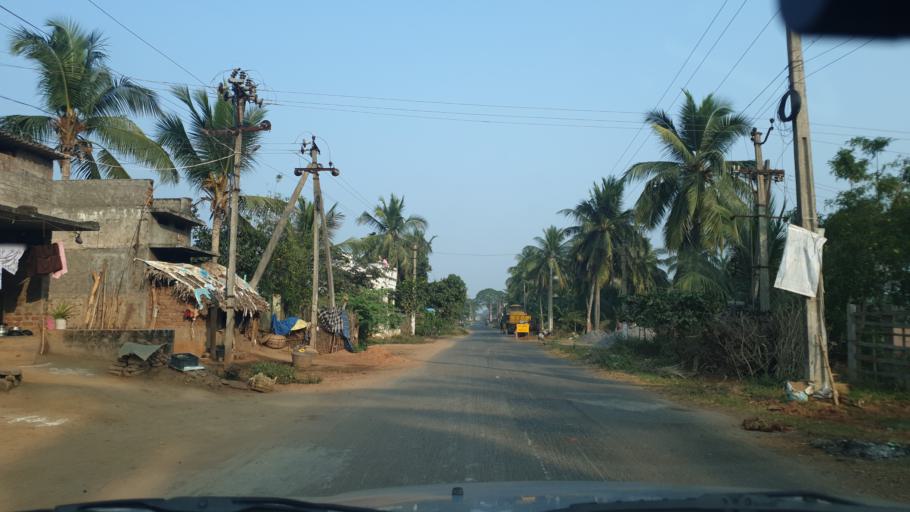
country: IN
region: Andhra Pradesh
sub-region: Srikakulam
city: Narasannapeta
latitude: 18.3316
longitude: 84.0401
